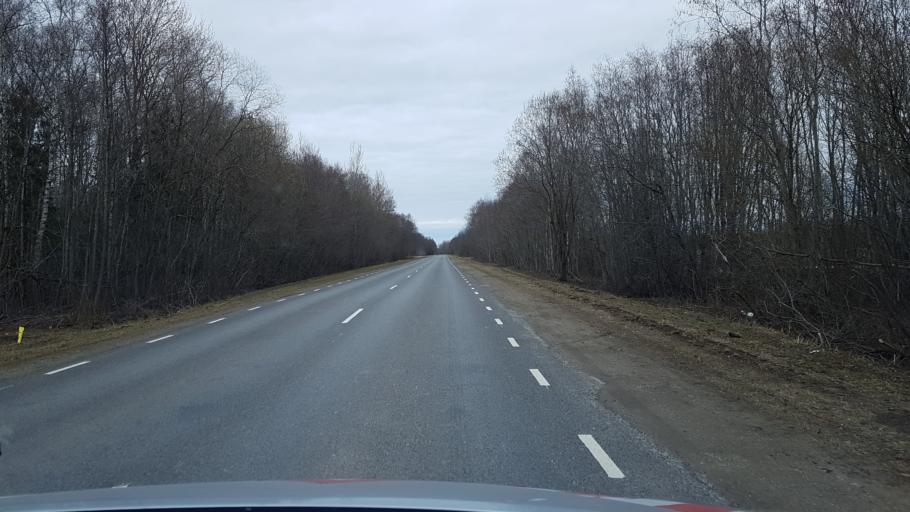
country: EE
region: Ida-Virumaa
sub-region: Sillamaee linn
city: Sillamae
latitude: 59.3555
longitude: 27.7481
